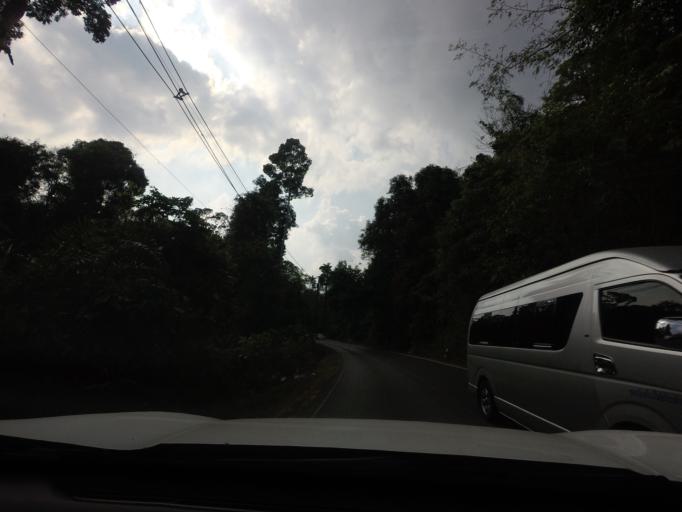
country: TH
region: Nakhon Ratchasima
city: Pak Chong
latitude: 14.4757
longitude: 101.3833
